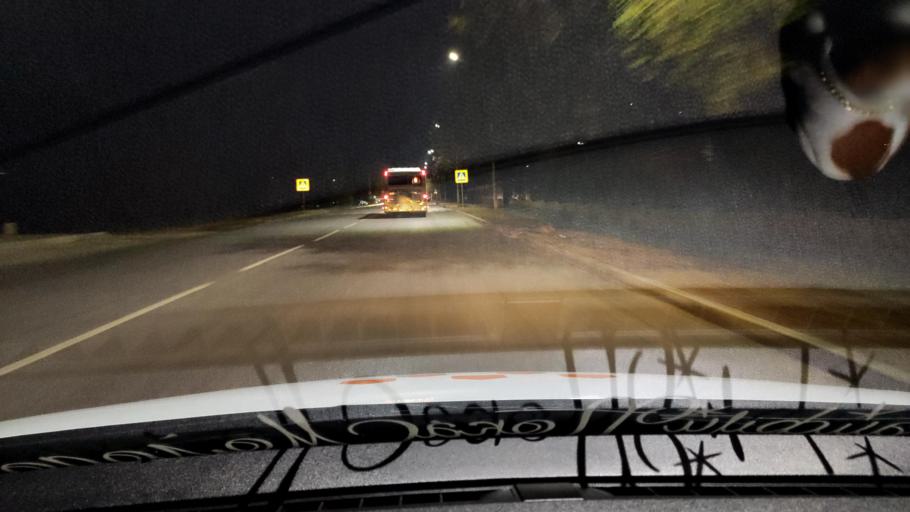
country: RU
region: Voronezj
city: Pridonskoy
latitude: 51.6492
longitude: 39.1002
